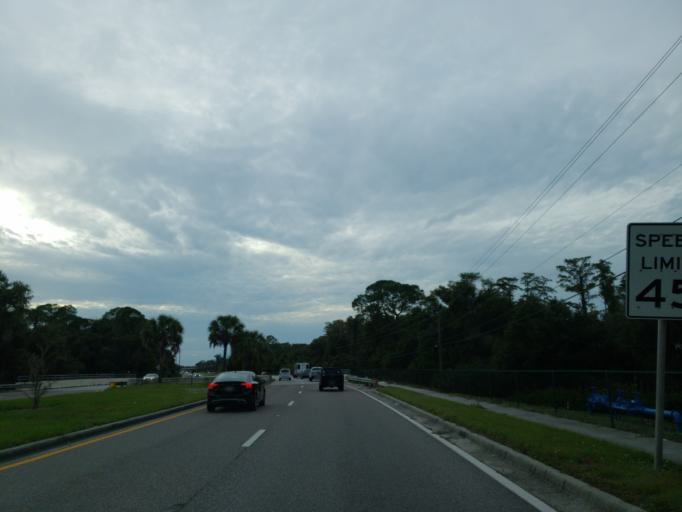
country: US
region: Florida
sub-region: Hillsborough County
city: Citrus Park
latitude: 28.0652
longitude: -82.5543
